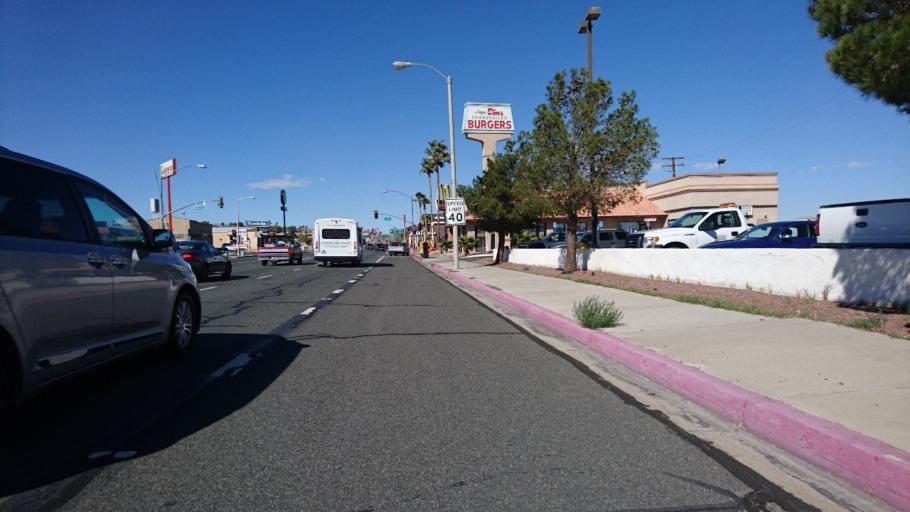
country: US
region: California
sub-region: San Bernardino County
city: Barstow
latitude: 34.8901
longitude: -116.9978
